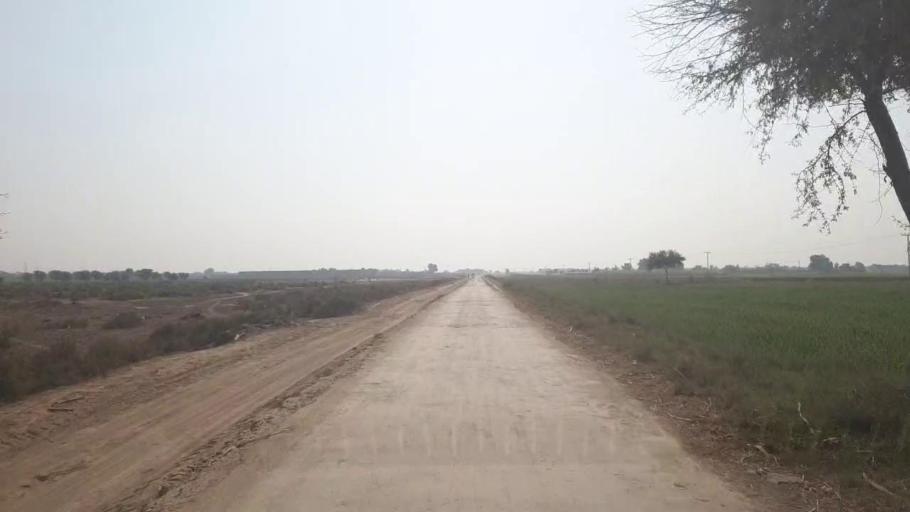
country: PK
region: Sindh
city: Tando Allahyar
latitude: 25.4765
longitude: 68.8056
